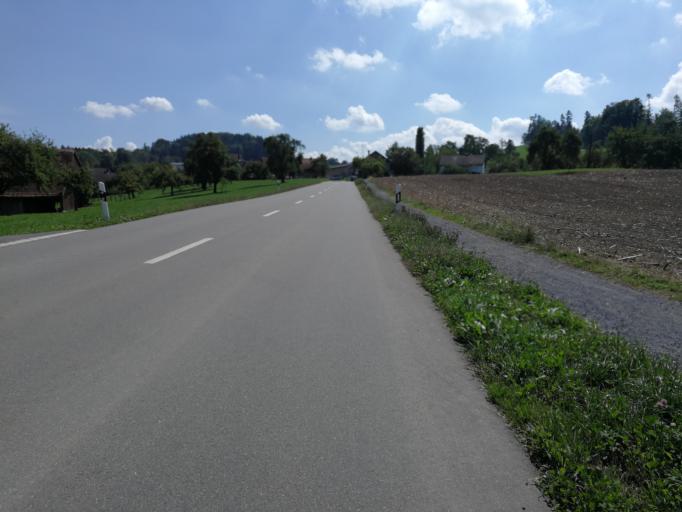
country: CH
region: Zurich
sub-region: Bezirk Horgen
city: Au / Unter-Dorf
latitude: 47.2439
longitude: 8.6234
